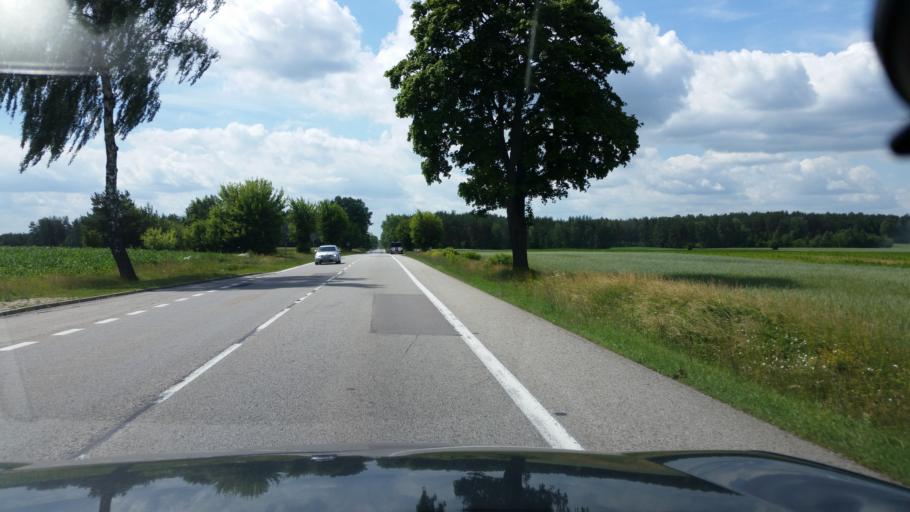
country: PL
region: Podlasie
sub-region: Powiat kolnenski
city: Stawiski
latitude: 53.2915
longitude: 22.1445
